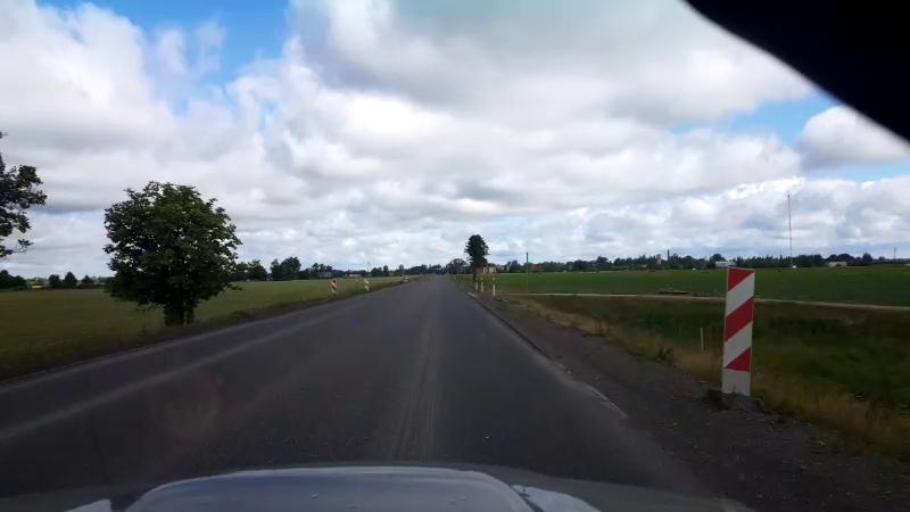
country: LV
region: Bauskas Rajons
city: Bauska
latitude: 56.3030
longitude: 24.3421
